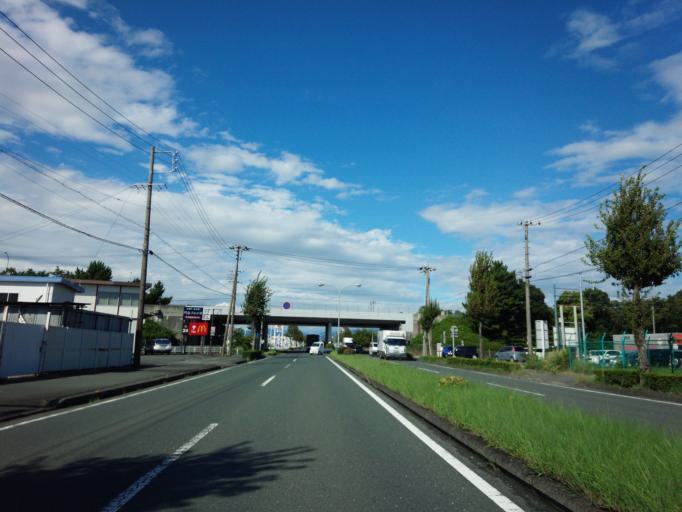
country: JP
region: Shizuoka
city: Hamakita
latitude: 34.7469
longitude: 137.7909
